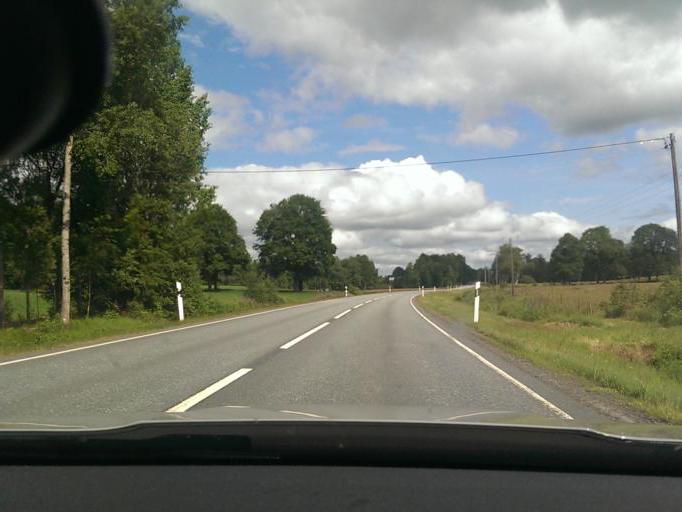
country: SE
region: Joenkoeping
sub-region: Varnamo Kommun
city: Varnamo
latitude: 57.2266
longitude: 14.0075
